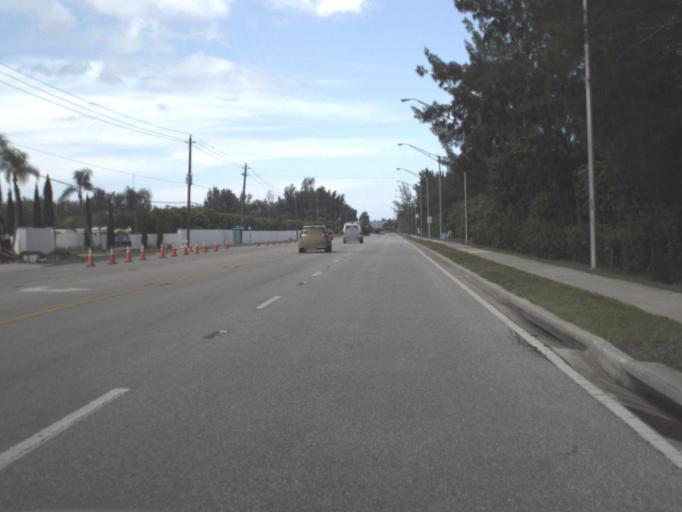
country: US
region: Florida
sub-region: Manatee County
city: Cortez
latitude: 27.4635
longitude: -82.6686
